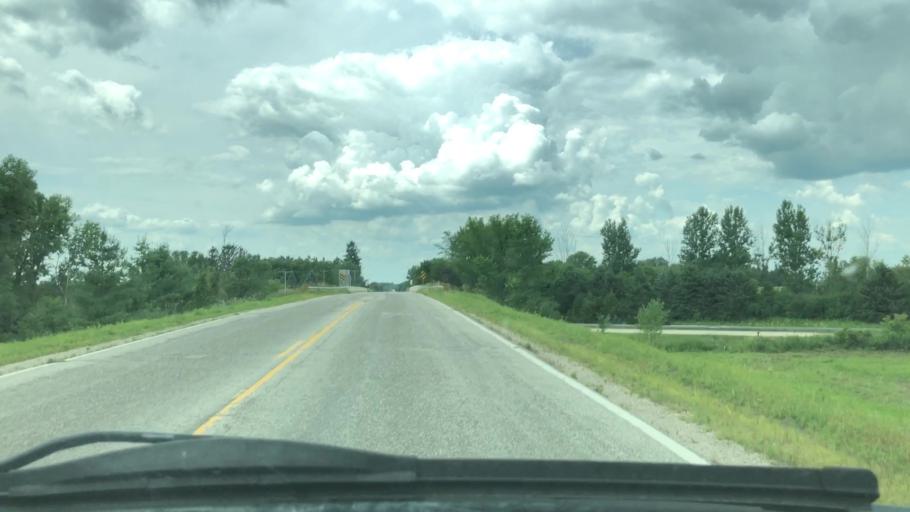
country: US
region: Minnesota
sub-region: Olmsted County
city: Stewartville
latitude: 43.8627
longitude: -92.5213
